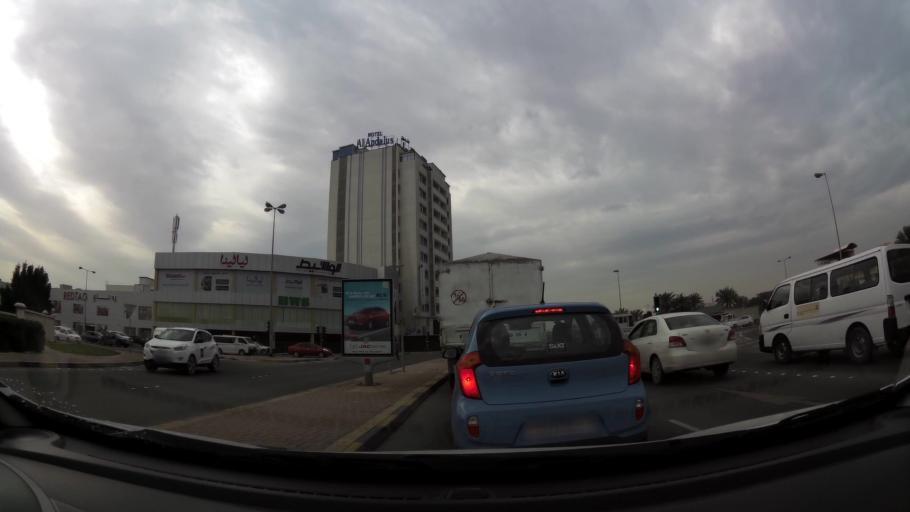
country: BH
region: Manama
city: Manama
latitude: 26.2212
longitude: 50.5853
